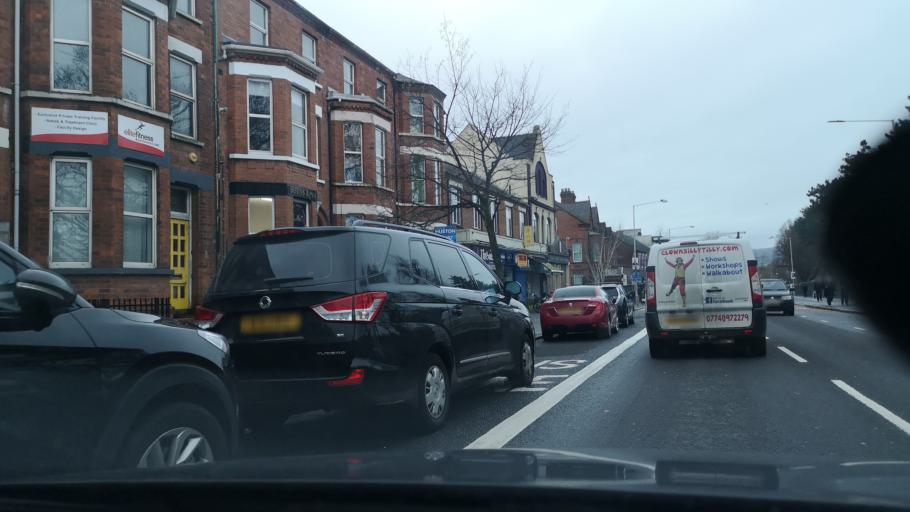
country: GB
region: Northern Ireland
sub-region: City of Belfast
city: Belfast
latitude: 54.5800
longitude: -5.9204
